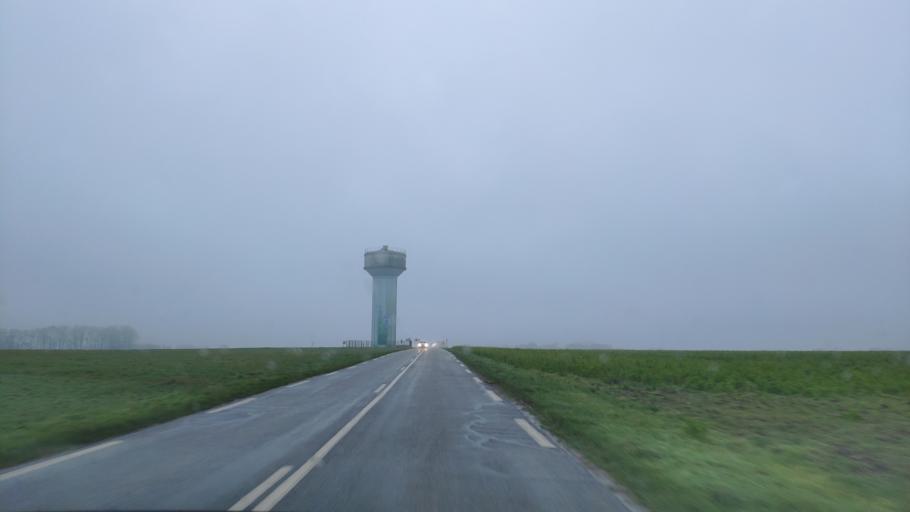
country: FR
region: Haute-Normandie
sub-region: Departement de la Seine-Maritime
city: Doudeville
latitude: 49.7130
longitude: 0.7372
